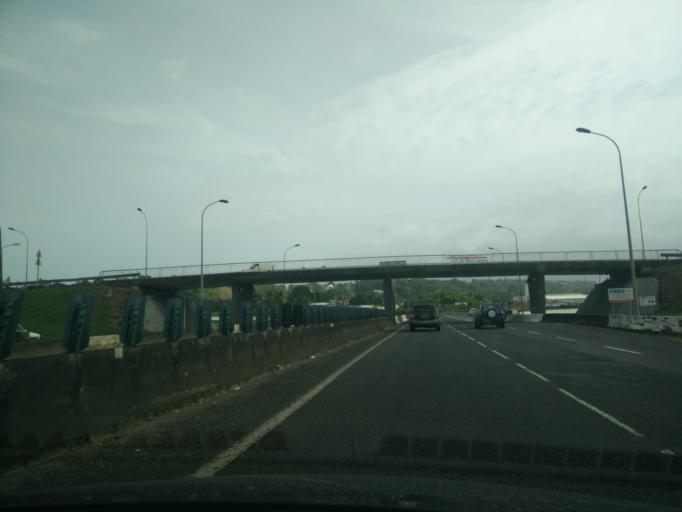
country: GP
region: Guadeloupe
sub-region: Guadeloupe
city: Petit-Bourg
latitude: 16.2030
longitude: -61.6055
